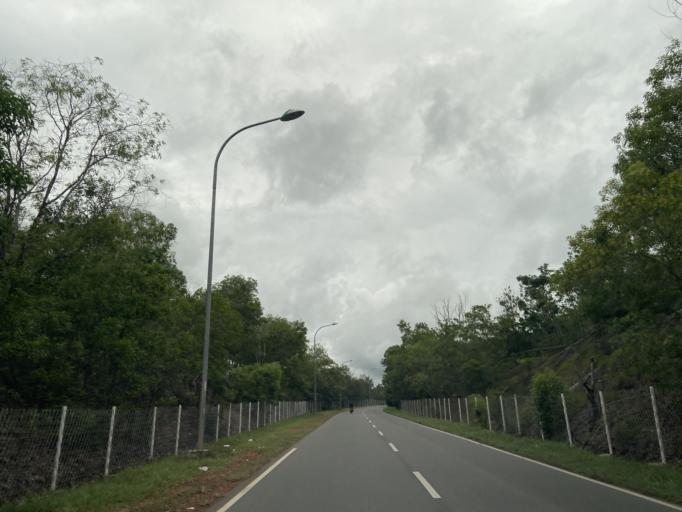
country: SG
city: Singapore
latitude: 1.1089
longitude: 104.0069
